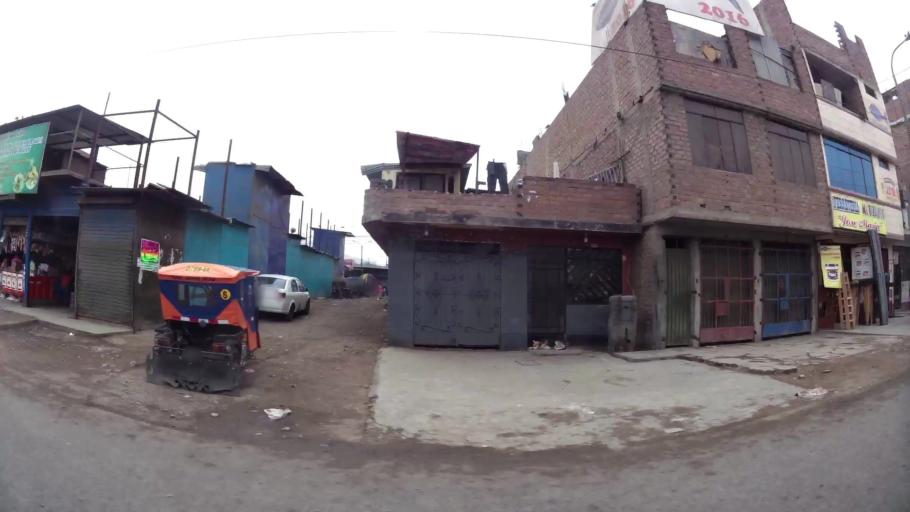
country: PE
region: Lima
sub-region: Lima
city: Independencia
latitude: -11.9456
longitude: -76.9787
